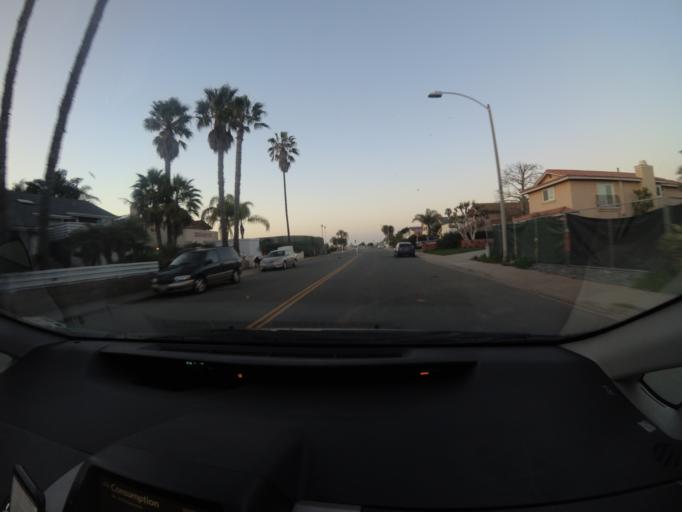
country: US
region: California
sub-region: San Diego County
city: Imperial Beach
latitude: 32.5749
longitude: -117.1225
